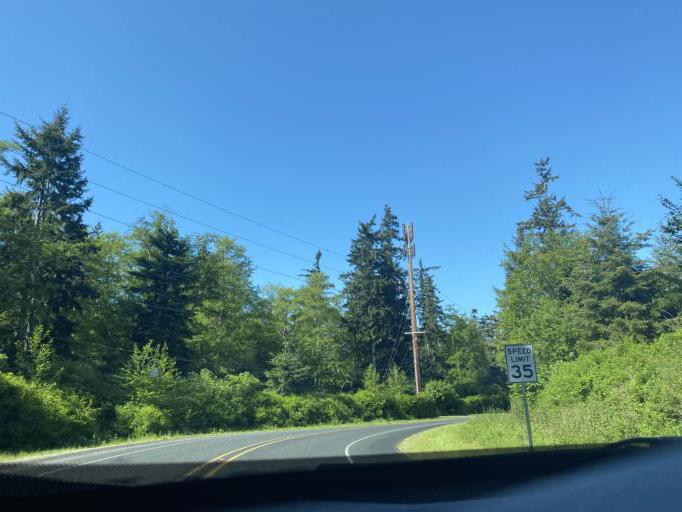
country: US
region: Washington
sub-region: Island County
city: Coupeville
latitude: 48.2085
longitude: -122.6672
